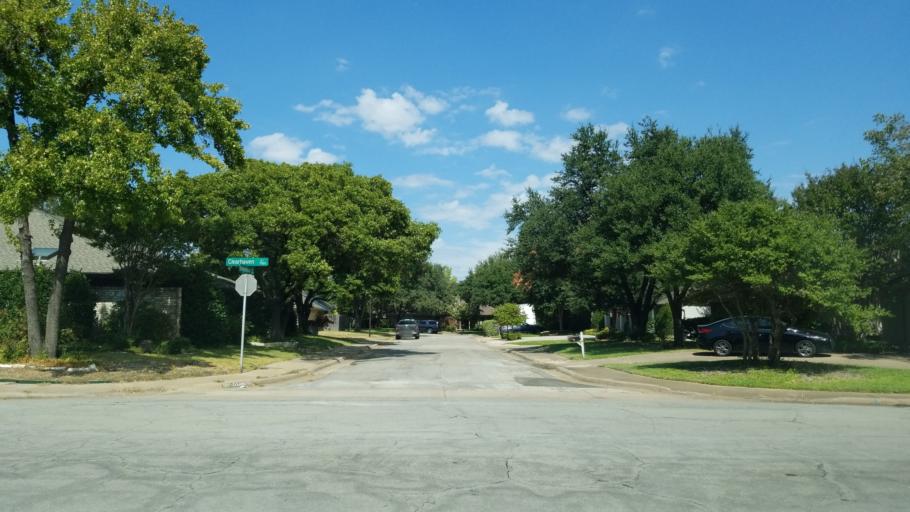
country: US
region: Texas
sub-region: Dallas County
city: Addison
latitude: 32.9668
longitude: -96.7870
